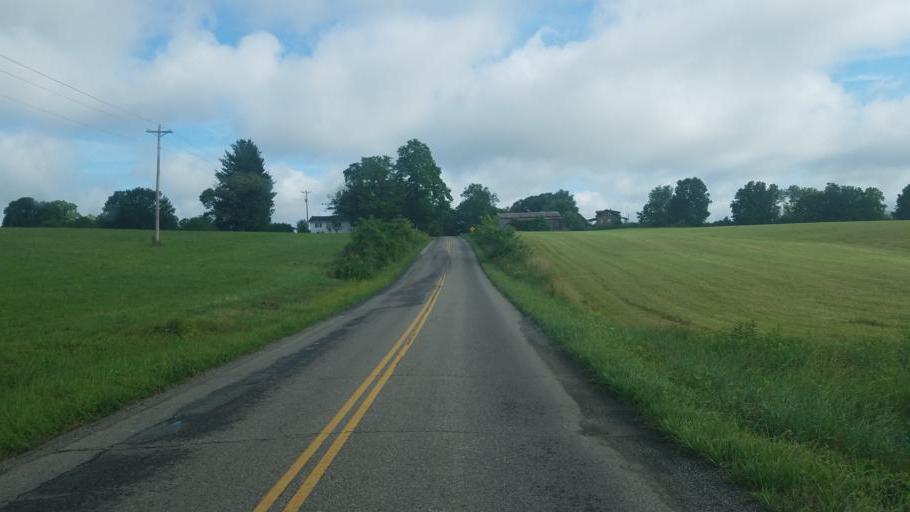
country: US
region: Ohio
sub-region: Gallia County
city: Gallipolis
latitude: 38.7866
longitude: -82.3949
